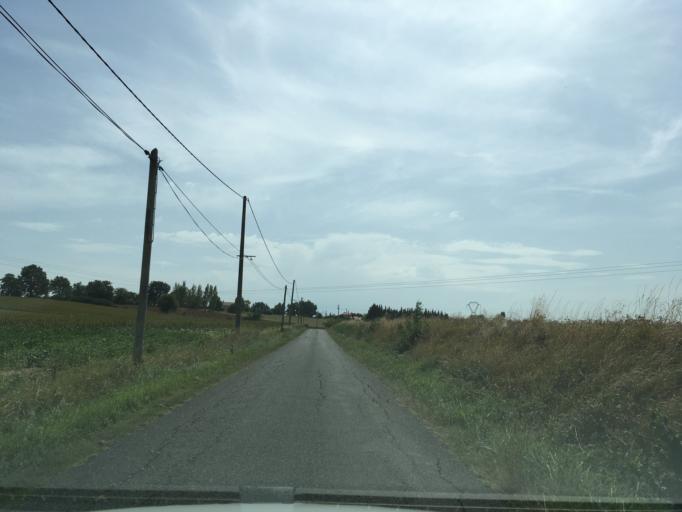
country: FR
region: Midi-Pyrenees
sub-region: Departement du Tarn
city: Castres
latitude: 43.6462
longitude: 2.2315
